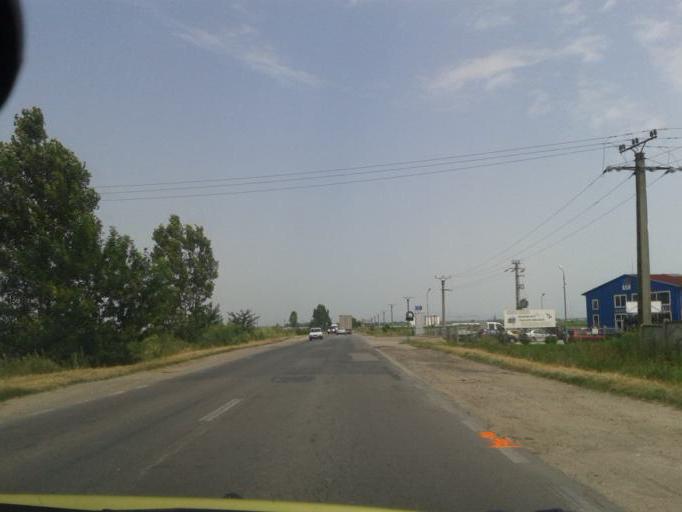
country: RO
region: Dambovita
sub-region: Oras Gaesti
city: Gaesti
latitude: 44.6862
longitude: 25.3138
